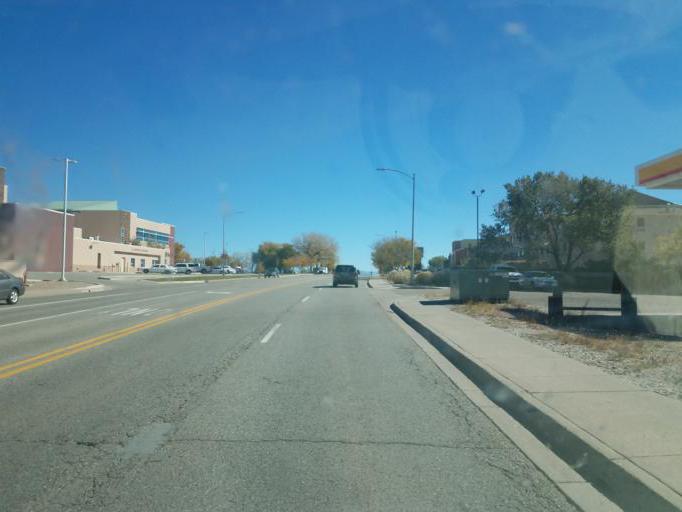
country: US
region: New Mexico
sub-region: Los Alamos County
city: Los Alamos
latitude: 35.8812
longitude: -106.3059
